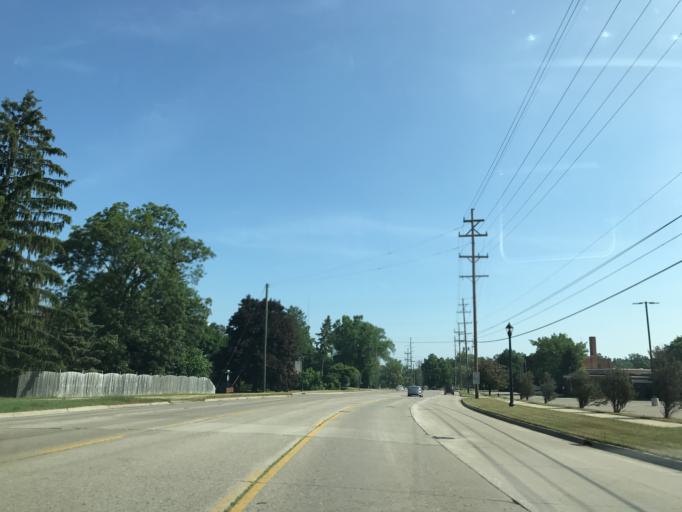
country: US
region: Michigan
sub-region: Ingham County
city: Okemos
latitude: 42.7098
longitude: -84.4323
